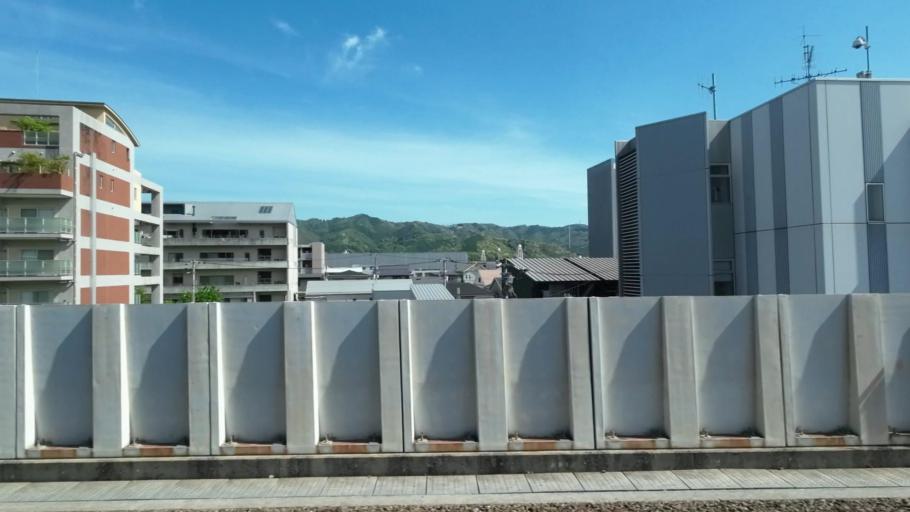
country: JP
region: Kochi
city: Kochi-shi
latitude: 33.5669
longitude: 133.5465
